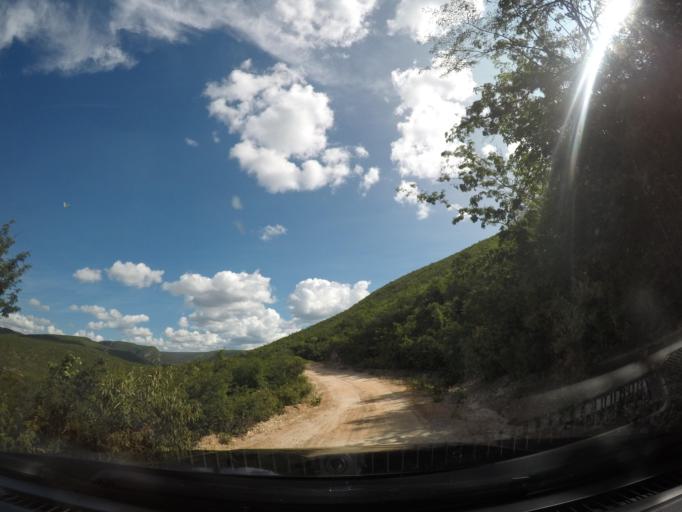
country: BR
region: Bahia
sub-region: Barra Da Estiva
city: Barra da Estiva
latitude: -13.2070
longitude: -41.5924
